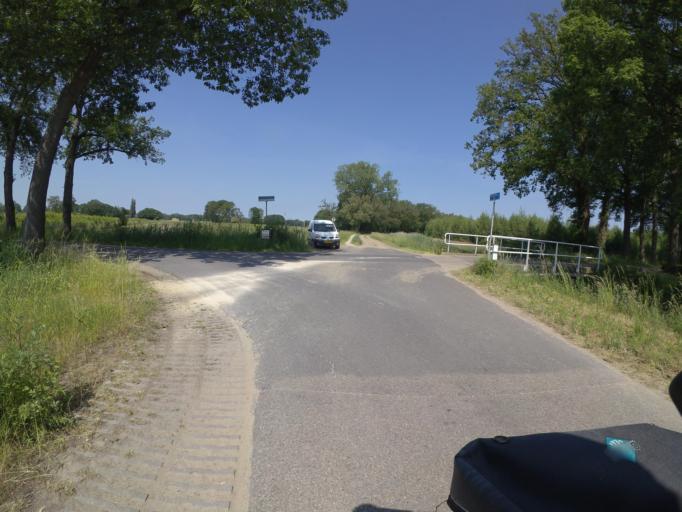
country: NL
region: Gelderland
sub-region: Berkelland
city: Neede
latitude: 52.1510
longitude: 6.6300
